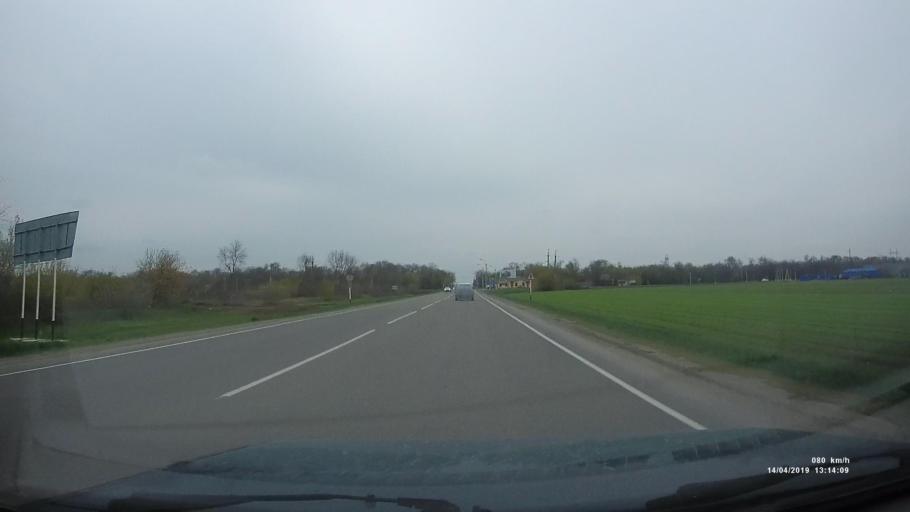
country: RU
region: Rostov
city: Kuleshovka
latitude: 47.0925
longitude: 39.6132
